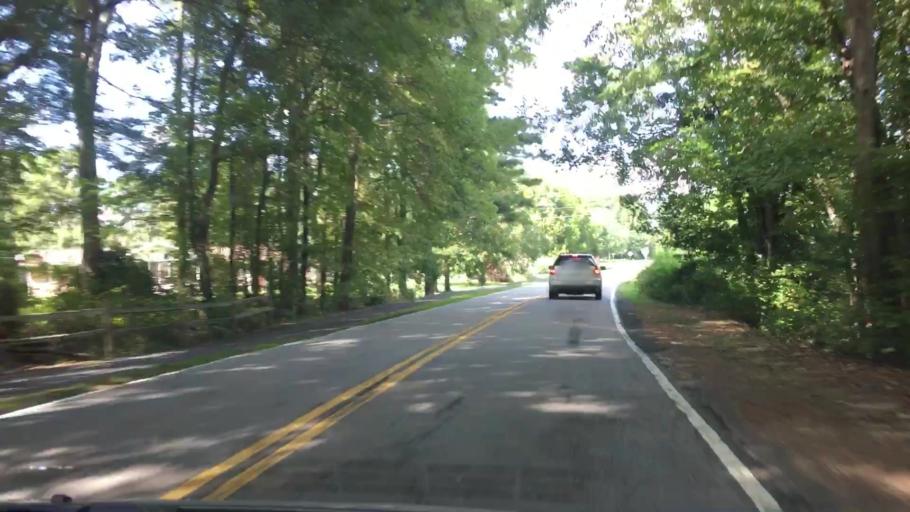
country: US
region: Georgia
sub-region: Fayette County
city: Fayetteville
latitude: 33.4368
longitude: -84.4597
